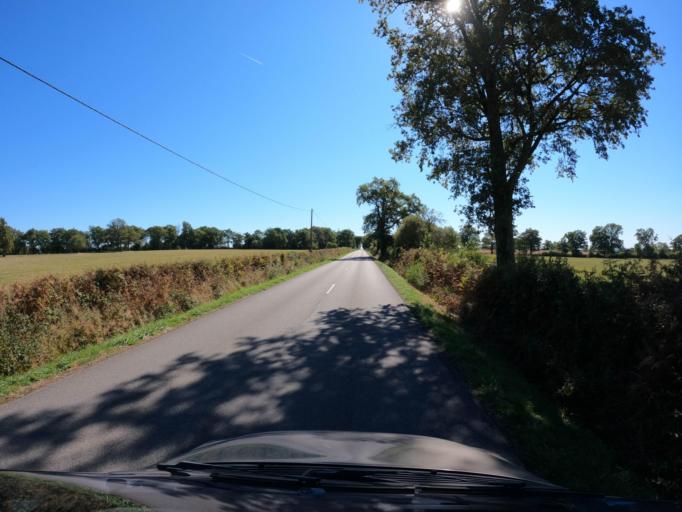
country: FR
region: Limousin
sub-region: Departement de la Haute-Vienne
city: Le Dorat
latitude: 46.2690
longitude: 1.0265
